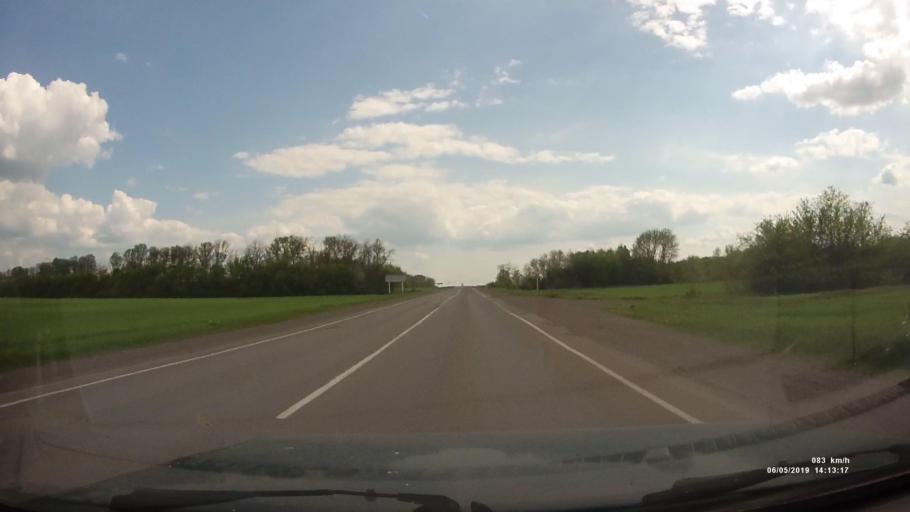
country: RU
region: Rostov
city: Kamenolomni
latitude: 47.6625
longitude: 40.2917
